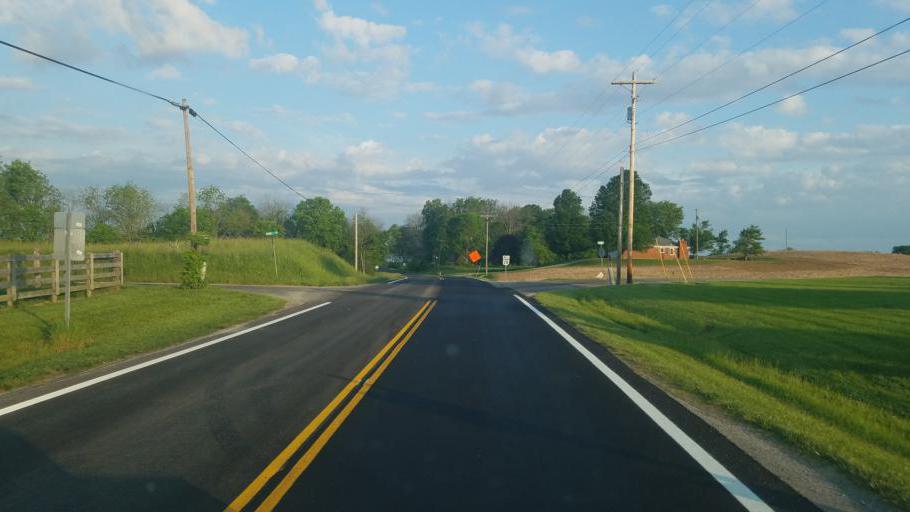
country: US
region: Ohio
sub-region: Highland County
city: Leesburg
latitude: 39.3577
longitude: -83.4781
